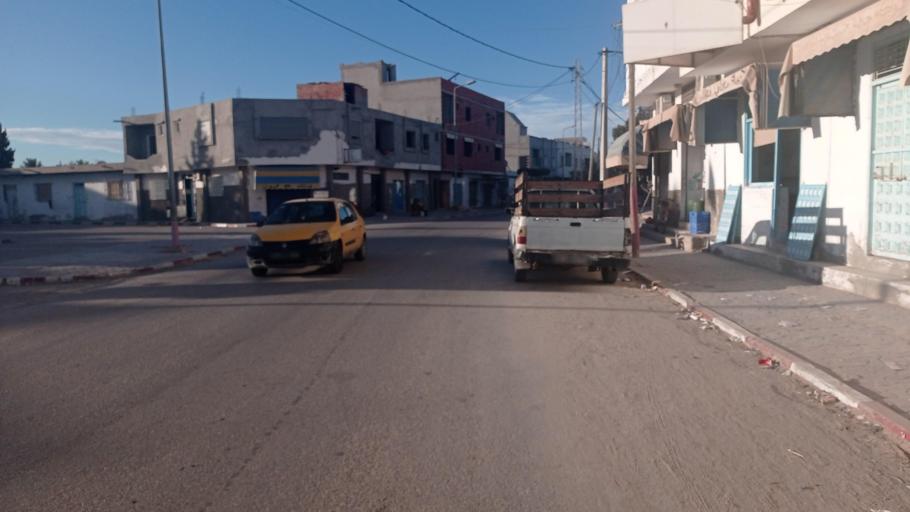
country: TN
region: Qabis
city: Gabes
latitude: 33.8413
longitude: 10.1176
